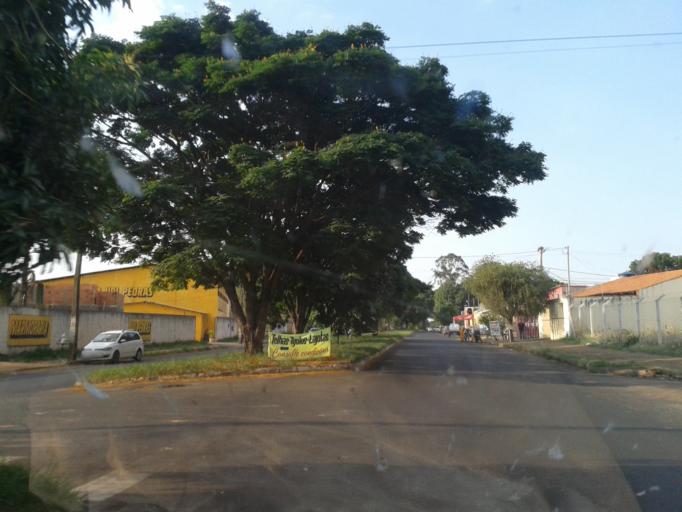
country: BR
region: Minas Gerais
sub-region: Uberlandia
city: Uberlandia
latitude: -18.9368
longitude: -48.3209
